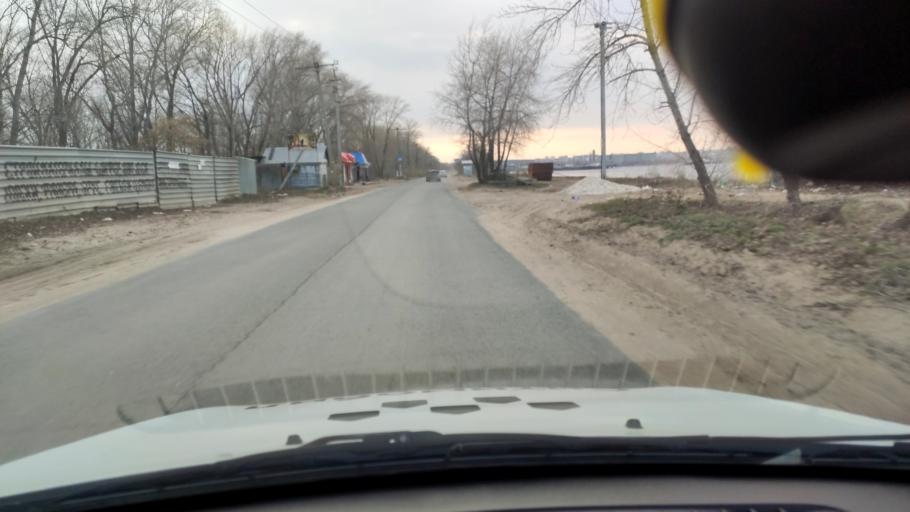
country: RU
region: Samara
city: Zhigulevsk
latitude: 53.4577
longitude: 49.5375
